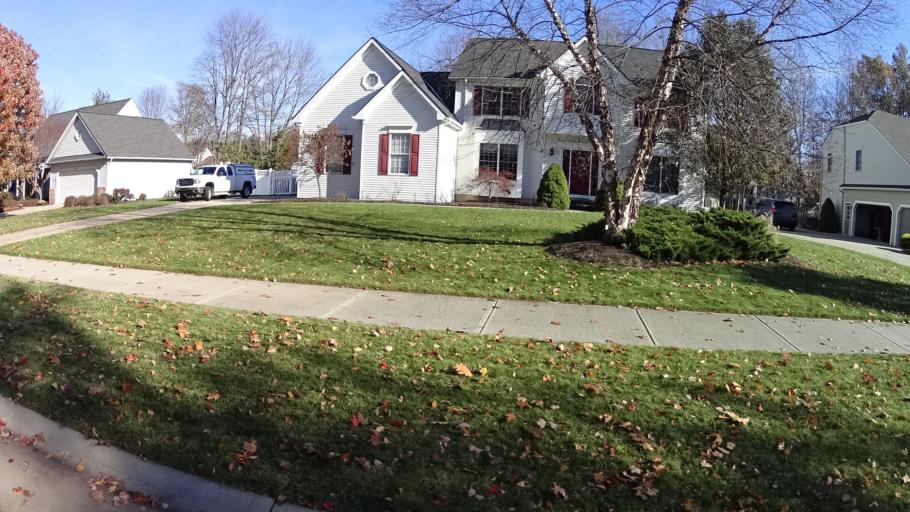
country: US
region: Ohio
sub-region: Lorain County
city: Avon Lake
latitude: 41.4968
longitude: -82.0080
